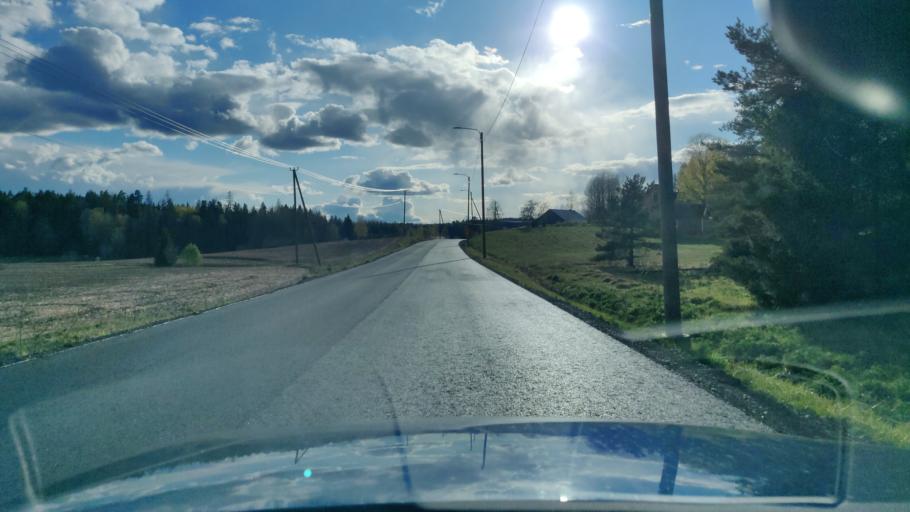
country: FI
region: Uusimaa
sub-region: Helsinki
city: Kauniainen
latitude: 60.3584
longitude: 24.7007
